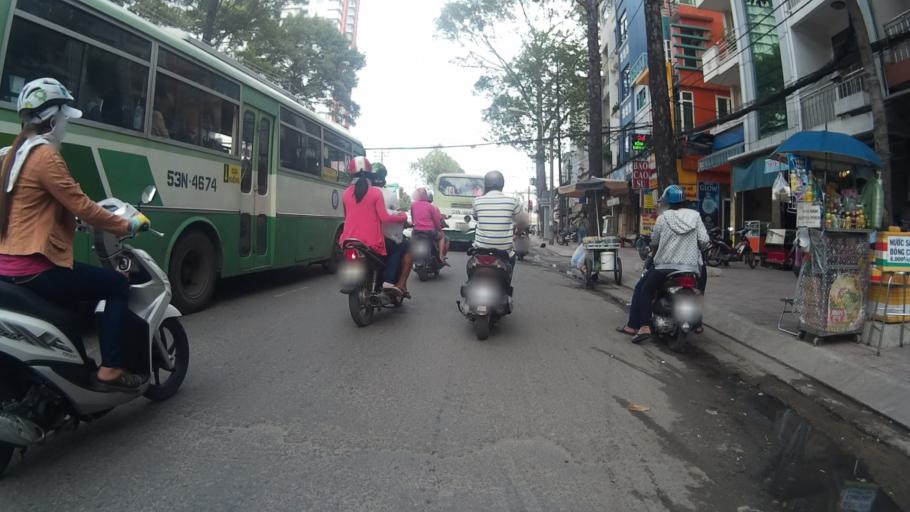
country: VN
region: Ho Chi Minh City
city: Quan Muoi
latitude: 10.7617
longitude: 106.6560
